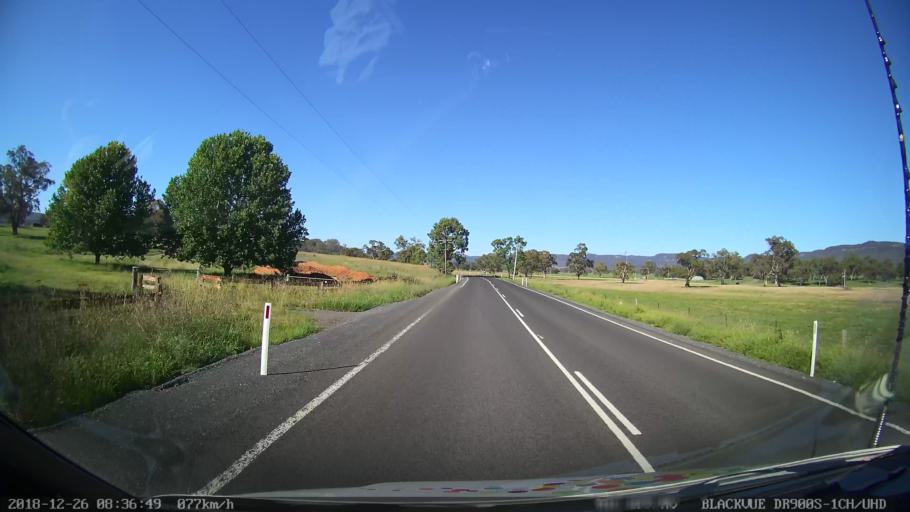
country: AU
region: New South Wales
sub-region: Upper Hunter Shire
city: Merriwa
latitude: -32.4262
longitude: 150.0957
